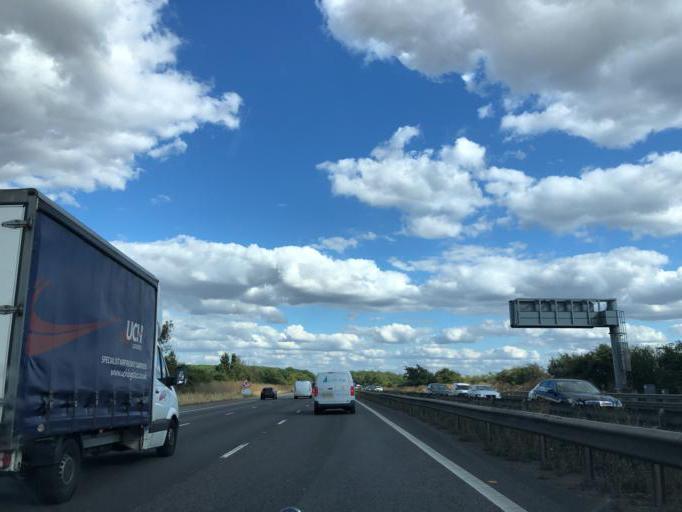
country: GB
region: England
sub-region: Milton Keynes
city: Stoke Goldington
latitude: 52.1144
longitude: -0.7966
